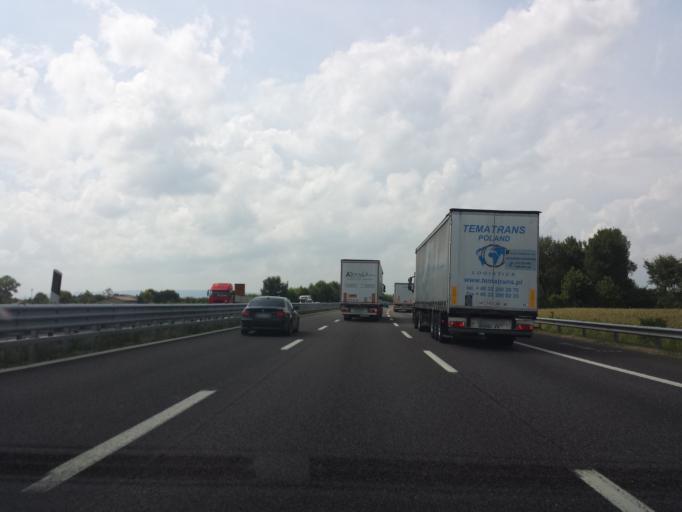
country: IT
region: Veneto
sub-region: Provincia di Padova
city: Bosco
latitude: 45.4559
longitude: 11.7933
